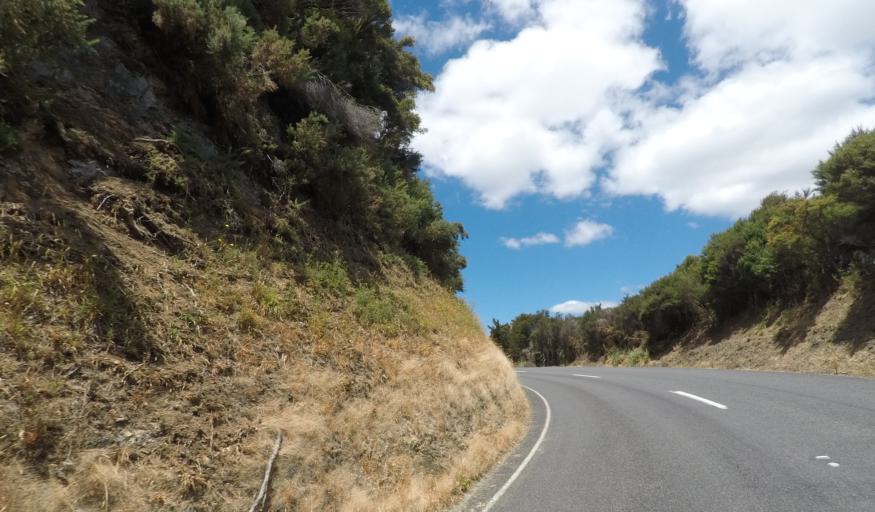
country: NZ
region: Northland
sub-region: Whangarei
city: Ngunguru
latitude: -35.5054
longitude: 174.4342
